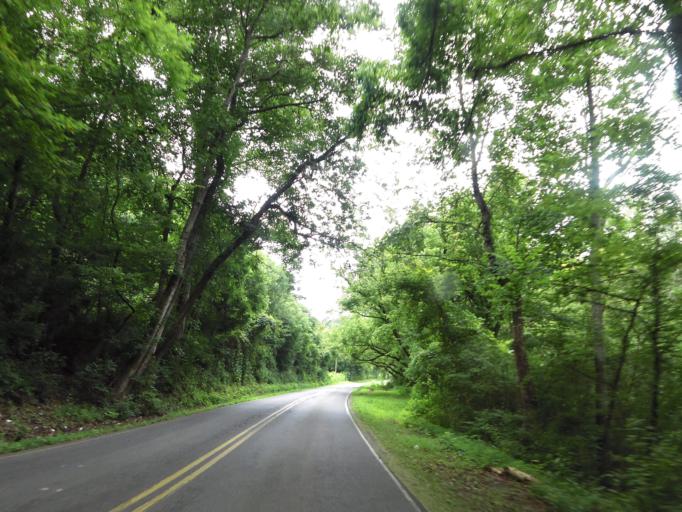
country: US
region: Tennessee
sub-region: Blount County
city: Eagleton Village
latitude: 35.8171
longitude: -83.9428
